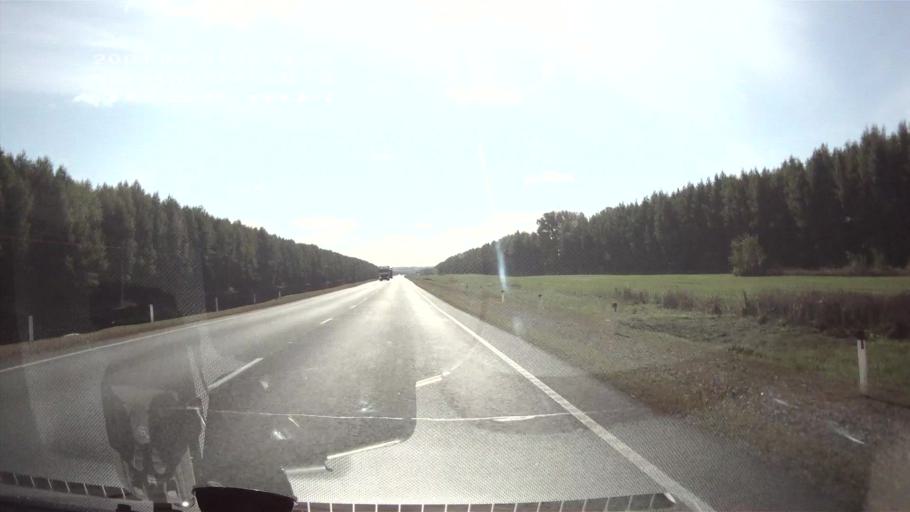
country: RU
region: Ulyanovsk
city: Tsil'na
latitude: 54.5465
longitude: 47.9497
